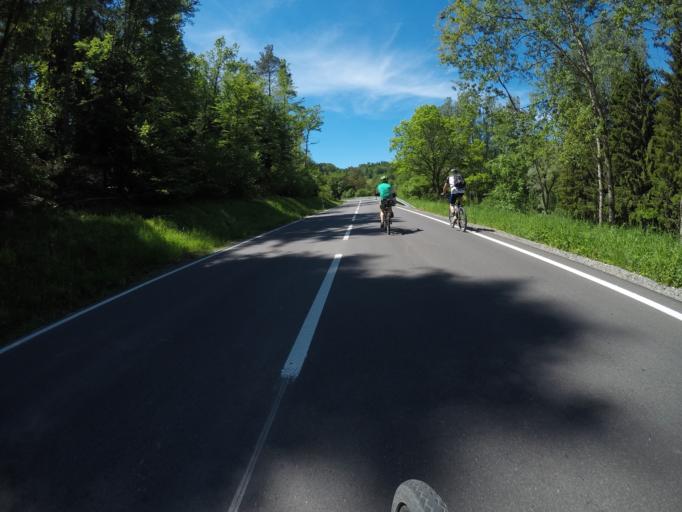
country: DE
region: Baden-Wuerttemberg
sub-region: Karlsruhe Region
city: Neuhausen
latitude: 48.8091
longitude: 8.8061
